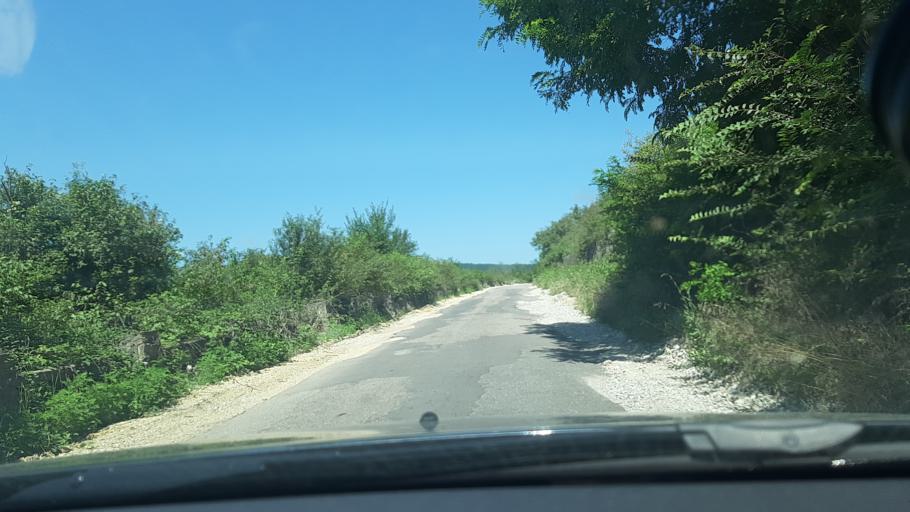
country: RO
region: Hunedoara
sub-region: Comuna Teliucu Inferior
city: Teliucu Inferior
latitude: 45.6893
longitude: 22.8756
